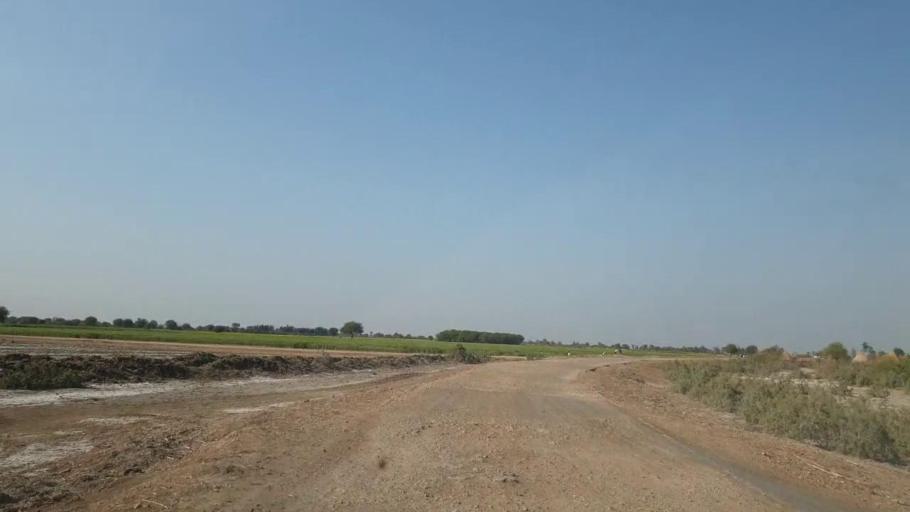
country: PK
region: Sindh
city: Tando Mittha Khan
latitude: 25.7598
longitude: 69.1939
